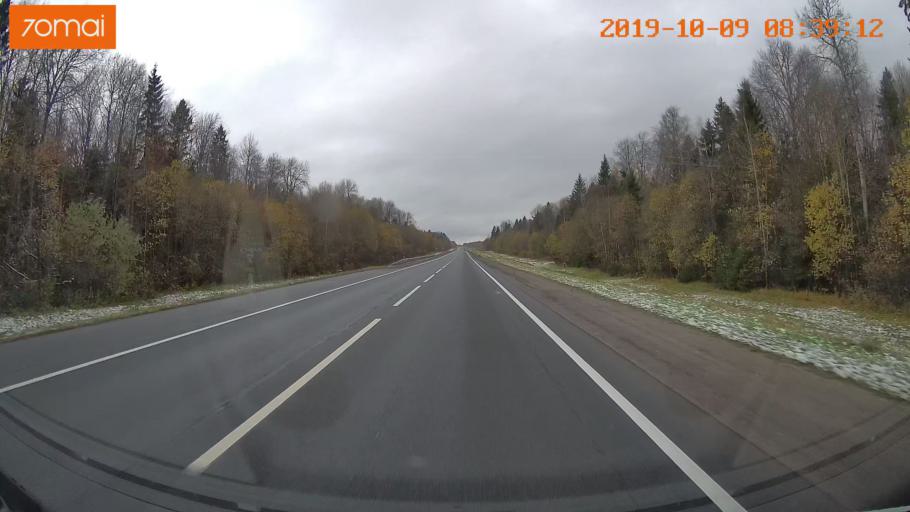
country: RU
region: Vologda
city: Gryazovets
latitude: 58.9677
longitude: 40.1562
